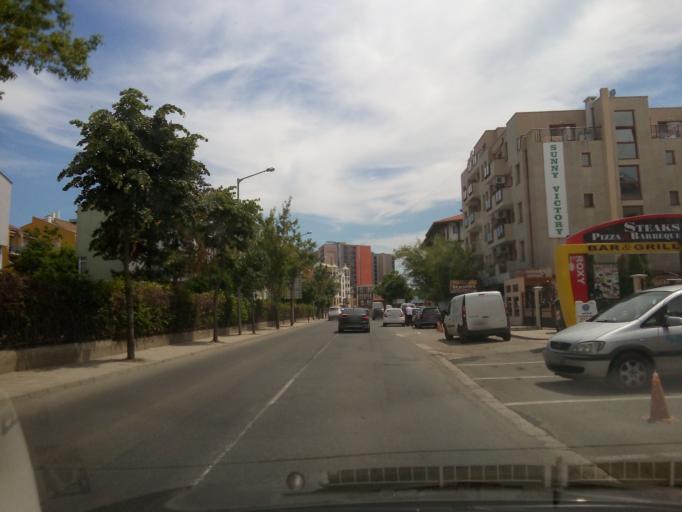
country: BG
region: Burgas
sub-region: Obshtina Nesebur
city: Sveti Vlas
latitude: 42.7094
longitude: 27.7217
